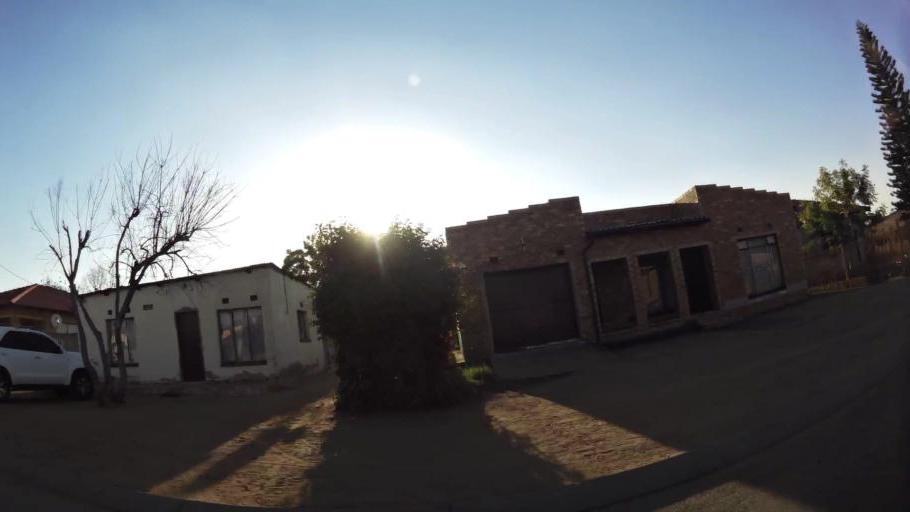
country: ZA
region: North-West
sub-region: Bojanala Platinum District Municipality
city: Rustenburg
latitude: -25.6417
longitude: 27.2155
